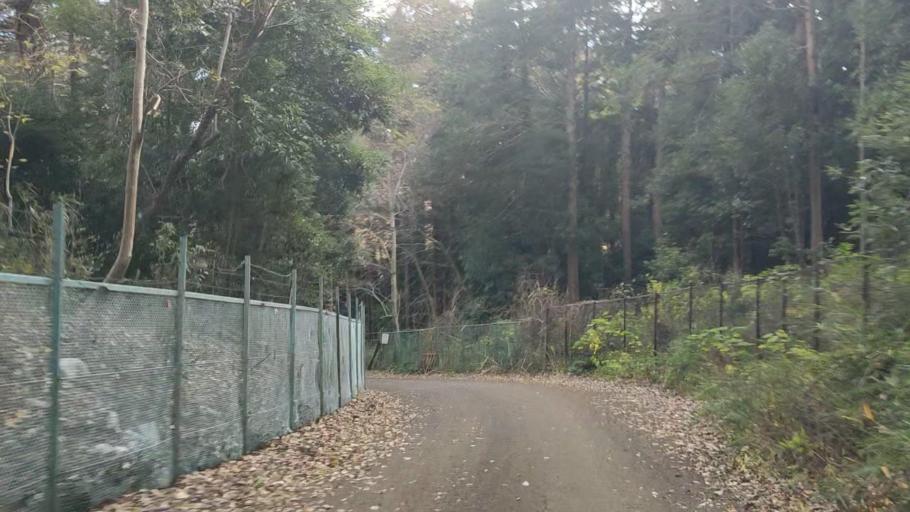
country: JP
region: Kanagawa
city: Minami-rinkan
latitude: 35.4836
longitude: 139.4985
